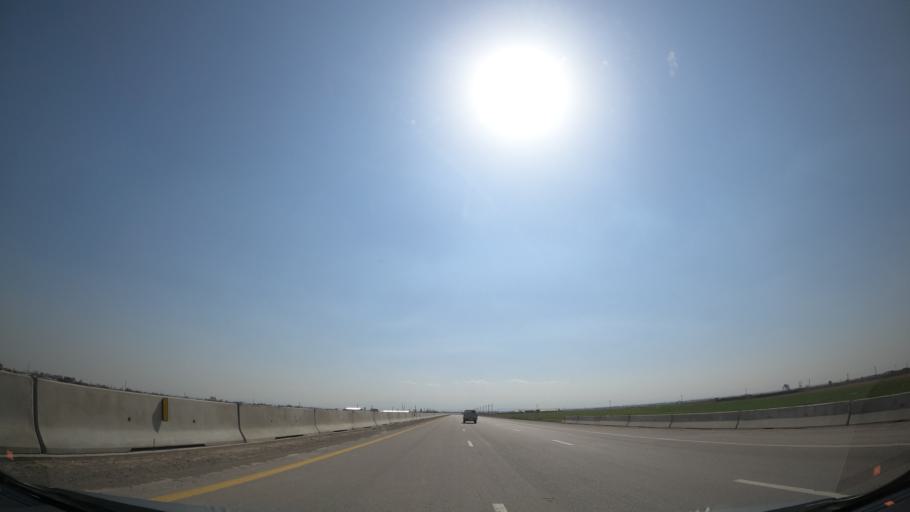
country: IR
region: Qazvin
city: Abyek
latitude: 35.9993
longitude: 50.4617
